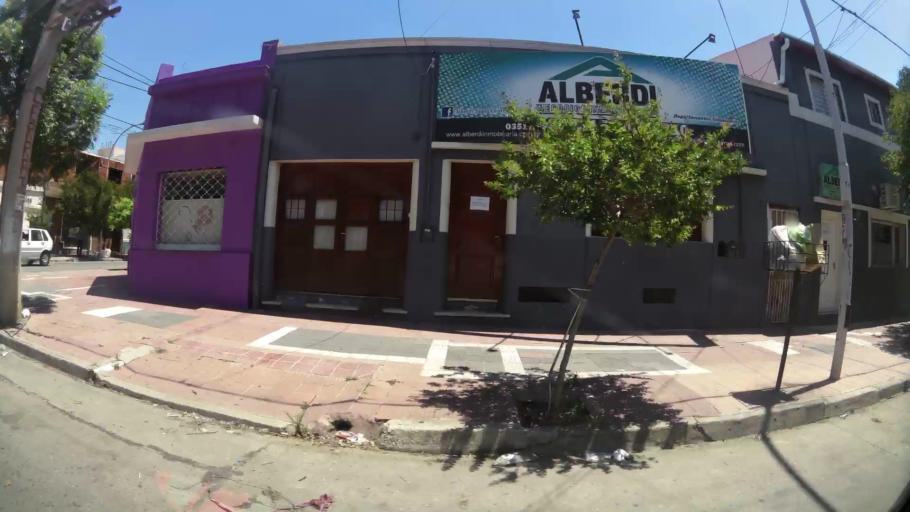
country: AR
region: Cordoba
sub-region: Departamento de Capital
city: Cordoba
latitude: -31.4049
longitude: -64.2191
